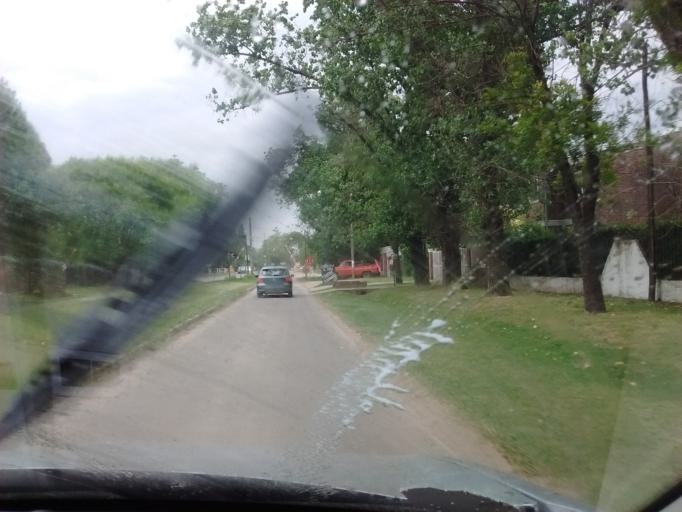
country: AR
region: Santa Fe
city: Funes
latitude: -32.9201
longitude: -60.7999
